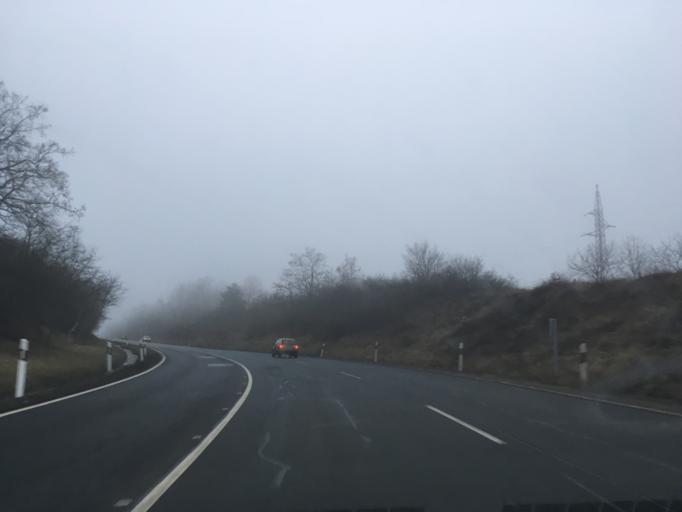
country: HU
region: Heves
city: Eger
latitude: 47.8679
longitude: 20.3795
